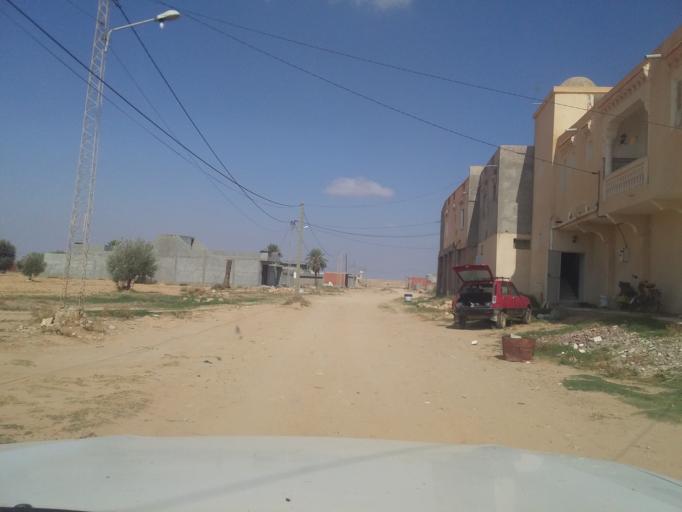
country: TN
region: Qabis
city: Matmata
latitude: 33.6202
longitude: 10.2693
